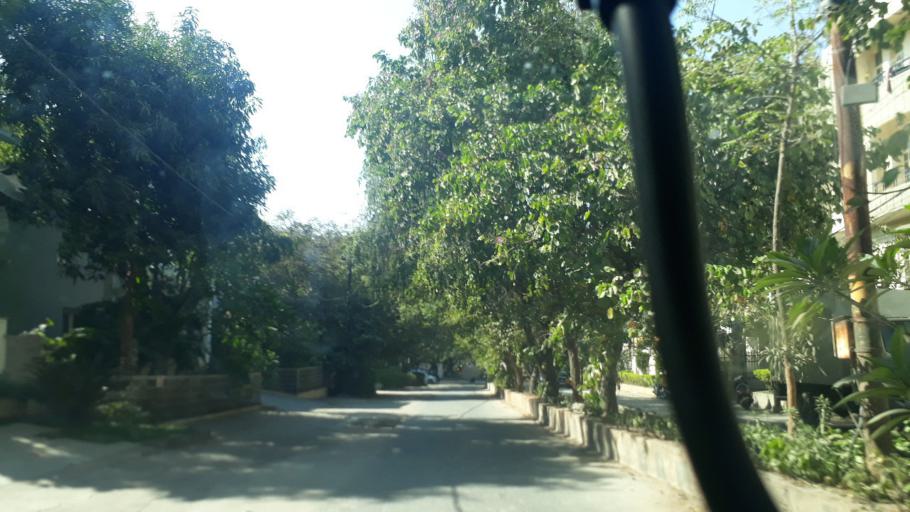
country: IN
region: Telangana
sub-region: Rangareddi
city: Kukatpalli
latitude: 17.4244
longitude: 78.4020
